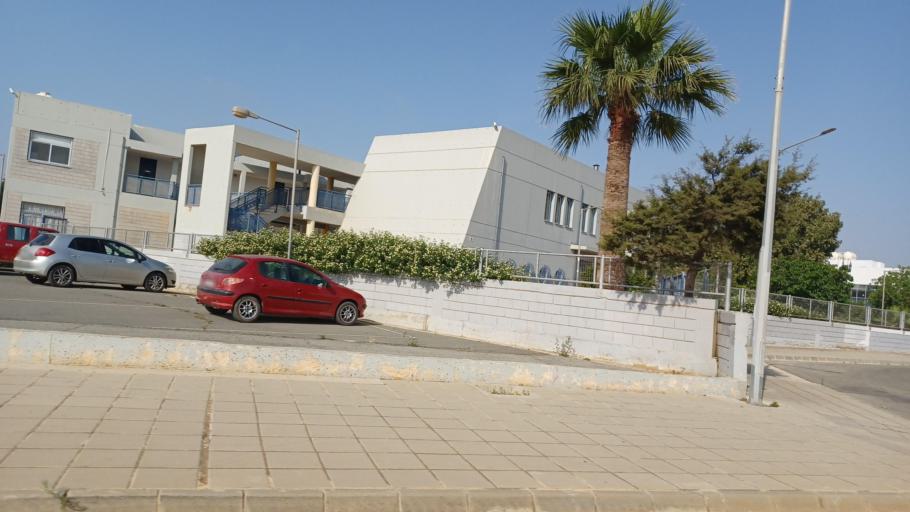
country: CY
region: Ammochostos
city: Avgorou
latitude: 35.0475
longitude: 33.8270
